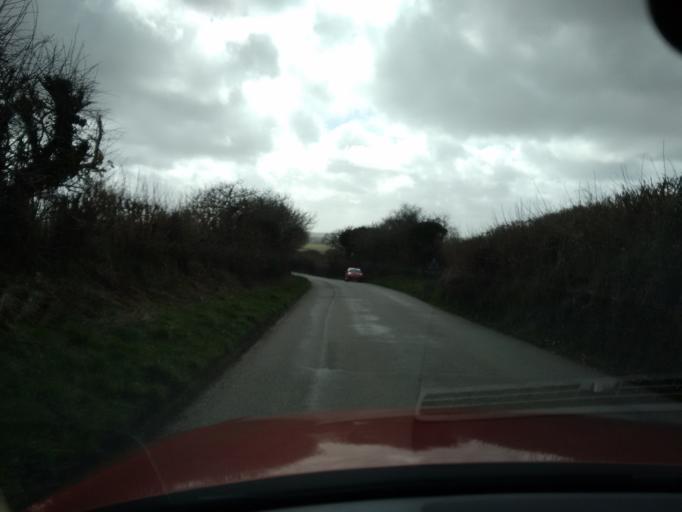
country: GB
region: England
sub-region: Cornwall
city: Liskeard
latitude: 50.4807
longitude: -4.5140
